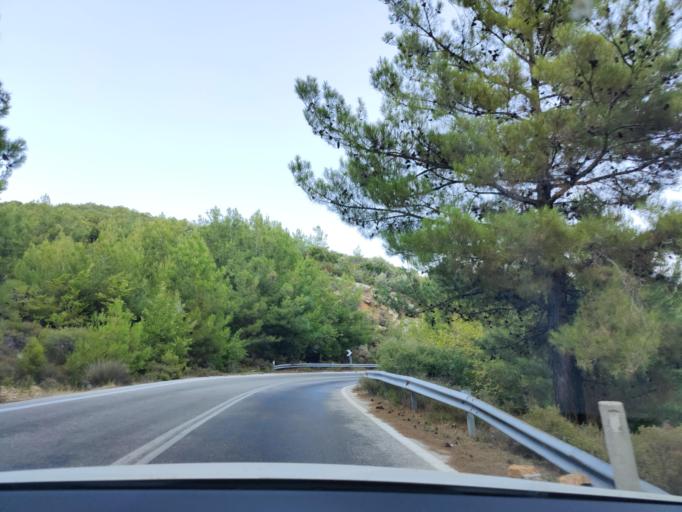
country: GR
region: East Macedonia and Thrace
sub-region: Nomos Kavalas
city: Potamia
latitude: 40.6251
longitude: 24.7621
